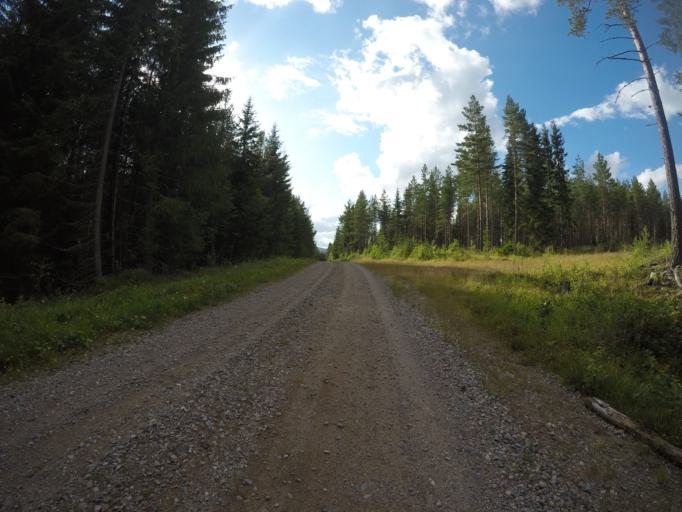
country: SE
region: OErebro
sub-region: Hallefors Kommun
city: Haellefors
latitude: 59.9740
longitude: 14.5598
